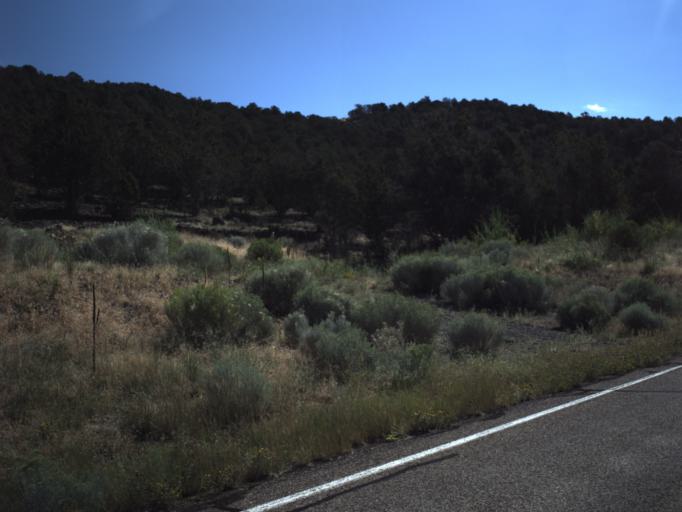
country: US
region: Utah
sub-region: Beaver County
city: Beaver
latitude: 38.2823
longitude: -112.5812
